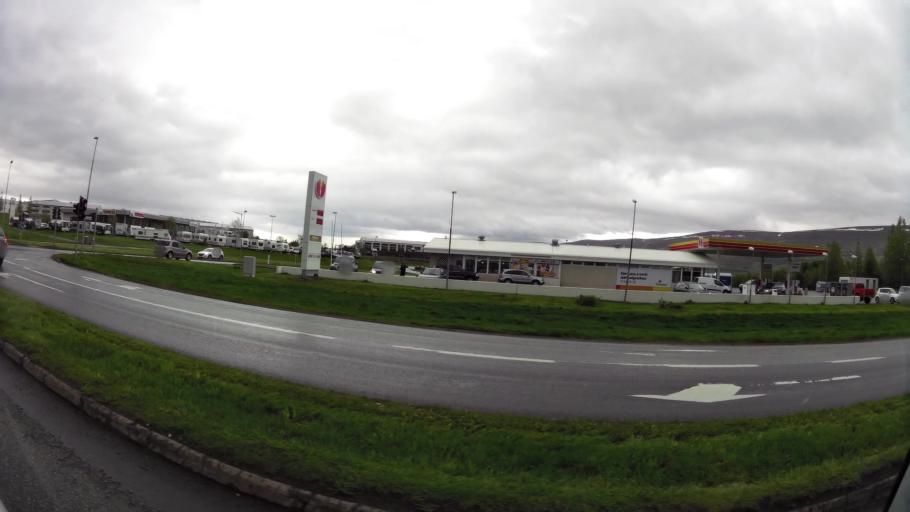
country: IS
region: Northeast
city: Akureyri
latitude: 65.6955
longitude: -18.1229
